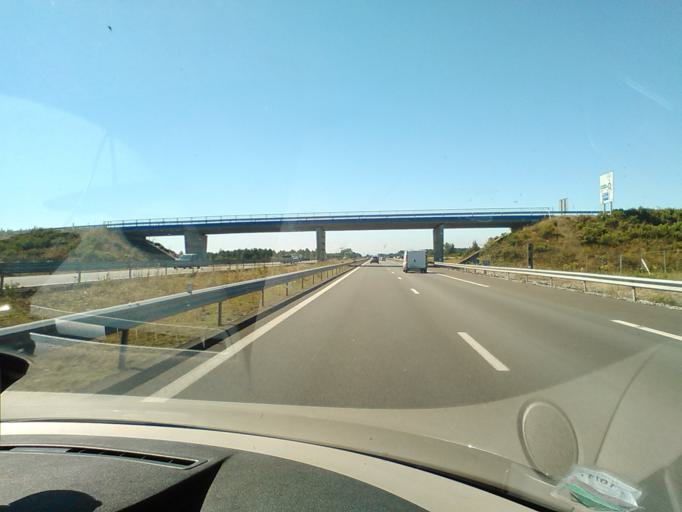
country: FR
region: Aquitaine
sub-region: Departement des Landes
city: Saint-Geours-de-Maremne
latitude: 43.7126
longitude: -1.2281
